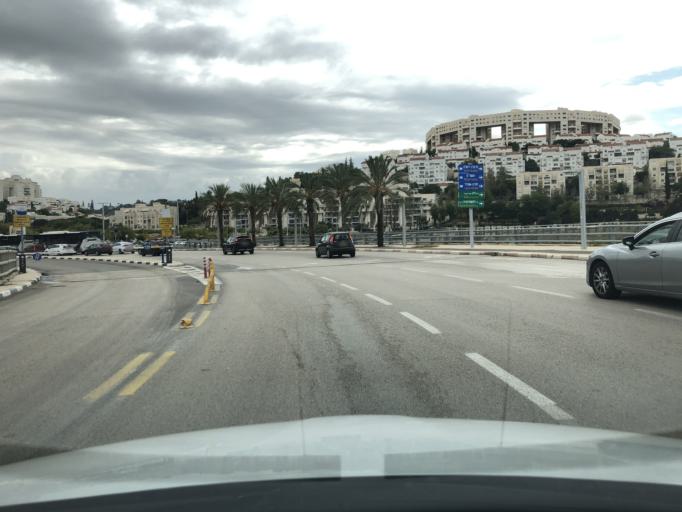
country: IL
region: Central District
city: Modiin
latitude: 31.8992
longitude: 35.0051
